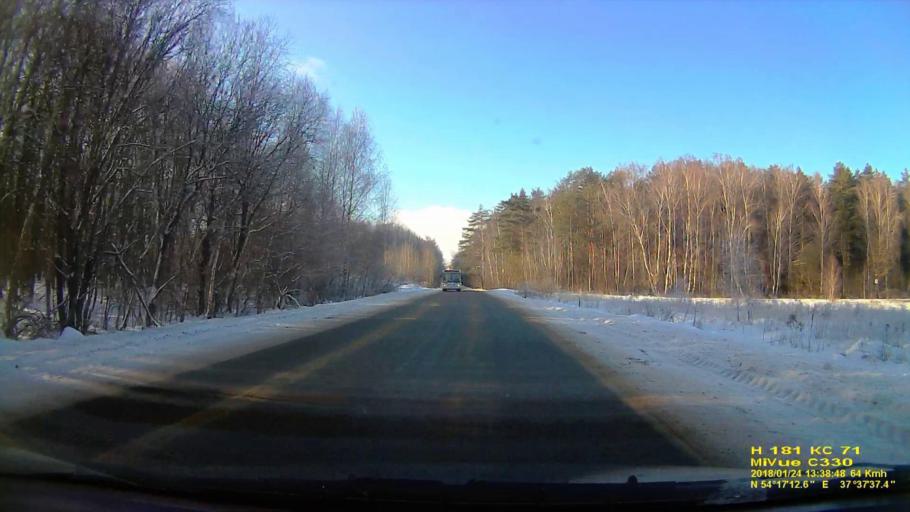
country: RU
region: Tula
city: Gorelki
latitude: 54.2869
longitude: 37.6268
